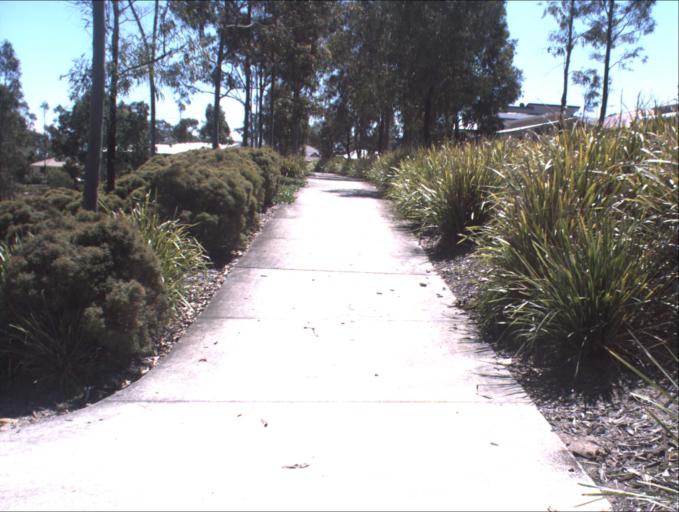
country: AU
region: Queensland
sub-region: Logan
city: Waterford West
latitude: -27.7066
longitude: 153.1576
